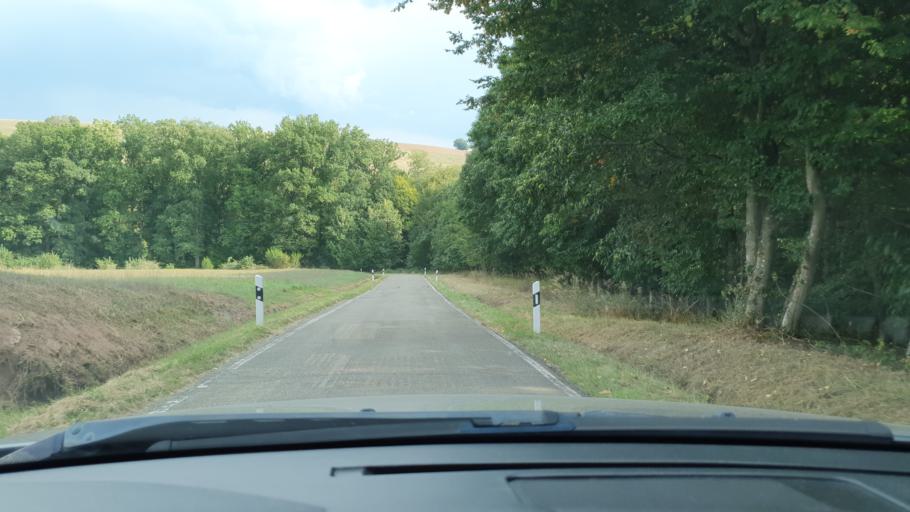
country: DE
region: Rheinland-Pfalz
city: Gerhardsbrunn
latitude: 49.3457
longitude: 7.5298
